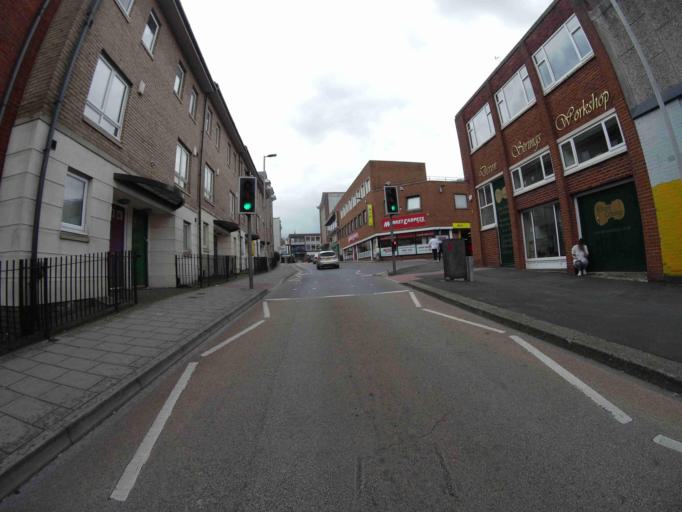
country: GB
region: England
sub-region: Devon
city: Exeter
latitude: 50.7212
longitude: -3.5325
